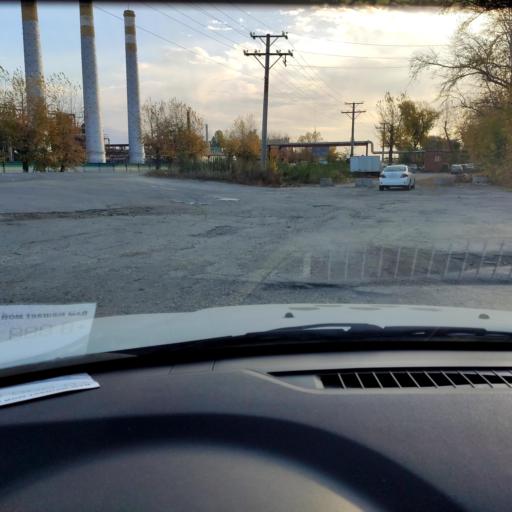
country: RU
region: Samara
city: Tol'yatti
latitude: 53.5342
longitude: 49.4435
